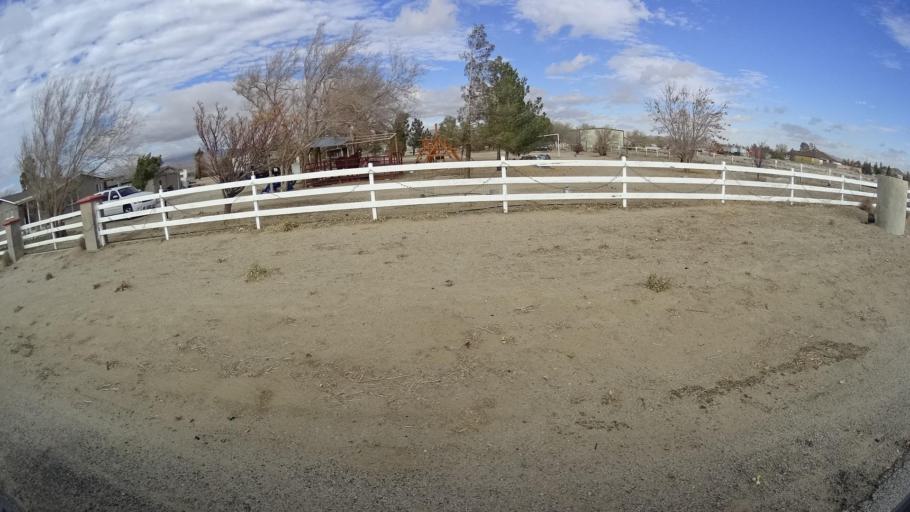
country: US
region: California
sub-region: Kern County
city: Rosamond
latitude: 34.8201
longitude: -118.2720
